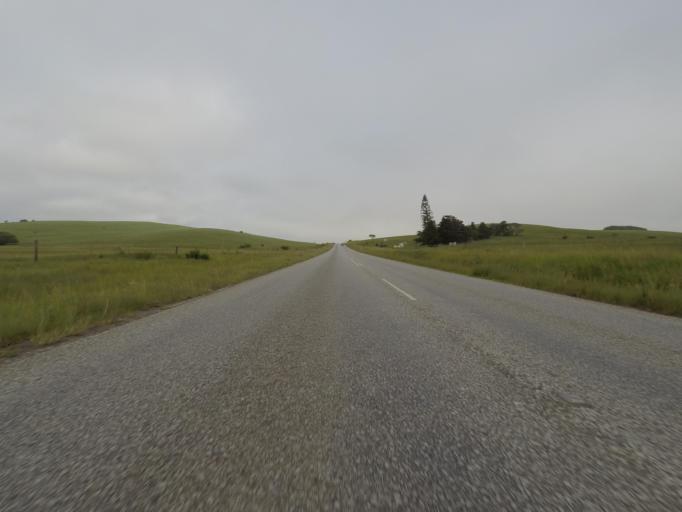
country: ZA
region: Eastern Cape
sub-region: Cacadu District Municipality
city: Port Alfred
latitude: -33.6085
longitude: 26.8155
